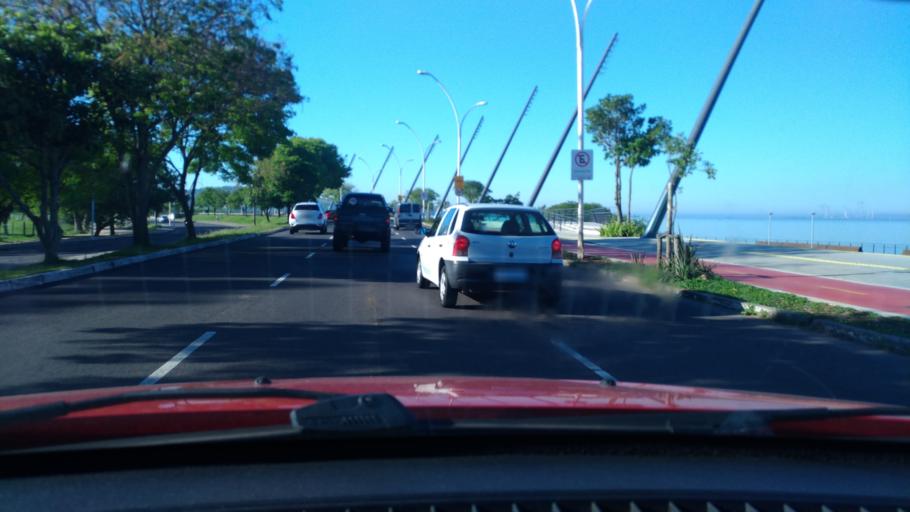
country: BR
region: Rio Grande do Sul
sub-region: Porto Alegre
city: Porto Alegre
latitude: -30.0394
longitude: -51.2413
